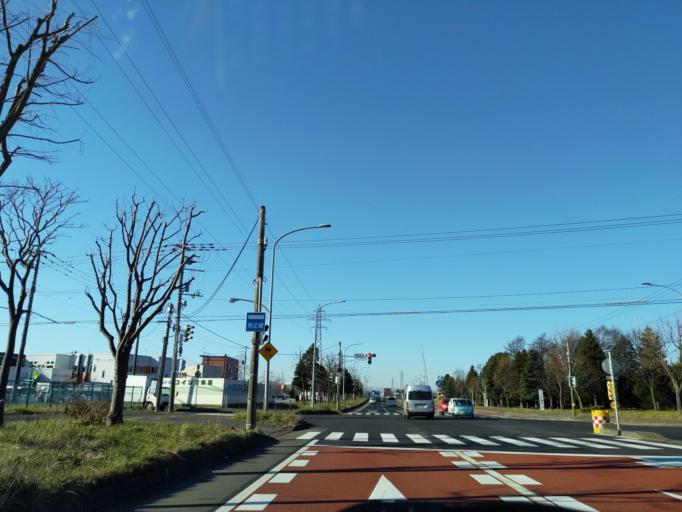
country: JP
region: Hokkaido
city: Kitahiroshima
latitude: 42.8946
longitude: 141.5906
